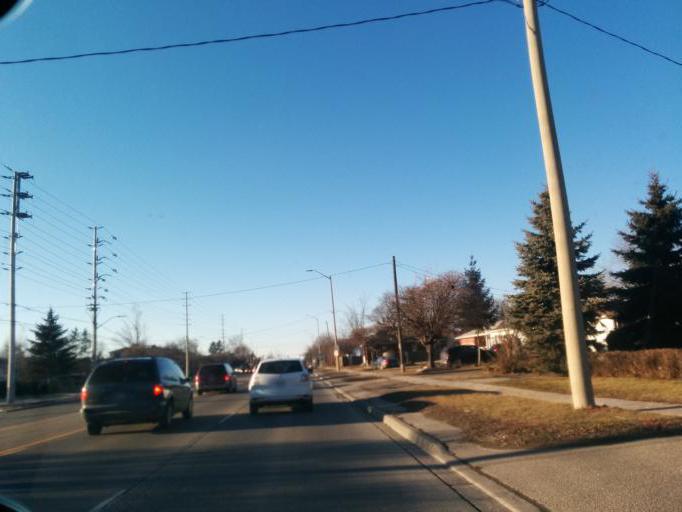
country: CA
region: Ontario
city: Mississauga
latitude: 43.5997
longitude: -79.6071
